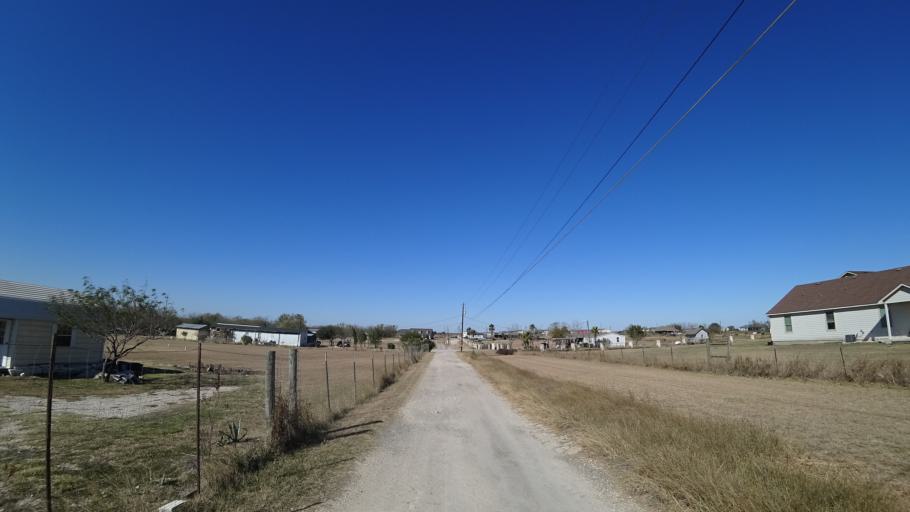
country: US
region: Texas
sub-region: Travis County
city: Garfield
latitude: 30.0975
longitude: -97.6200
